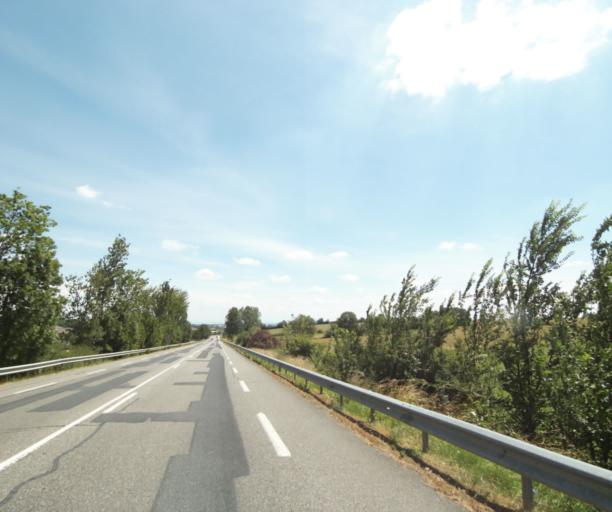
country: FR
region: Lorraine
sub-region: Departement de Meurthe-et-Moselle
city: Luneville
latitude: 48.6004
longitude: 6.4629
